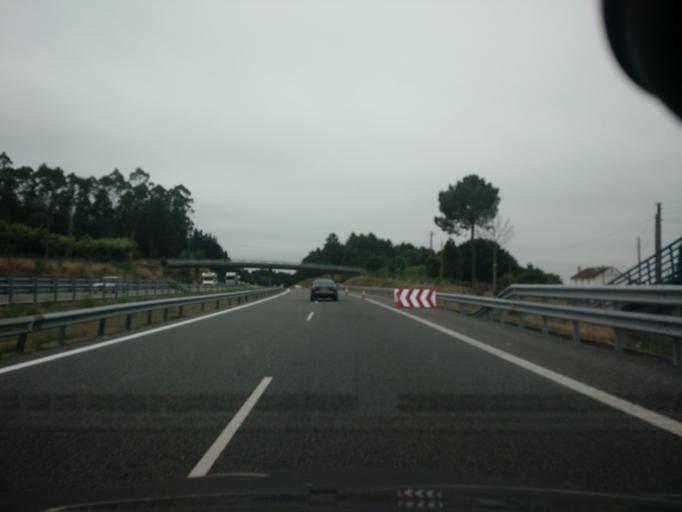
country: ES
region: Galicia
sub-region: Provincia da Coruna
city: Oroso
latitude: 42.9966
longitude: -8.4259
